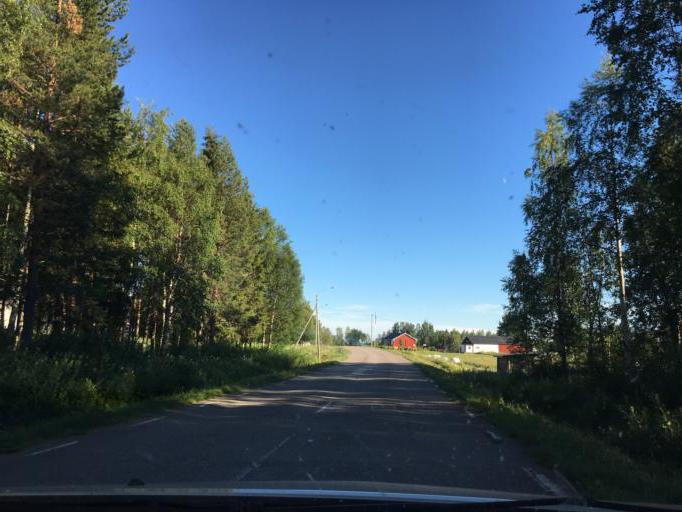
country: SE
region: Norrbotten
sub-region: Kalix Kommun
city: Rolfs
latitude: 65.9033
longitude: 22.9308
